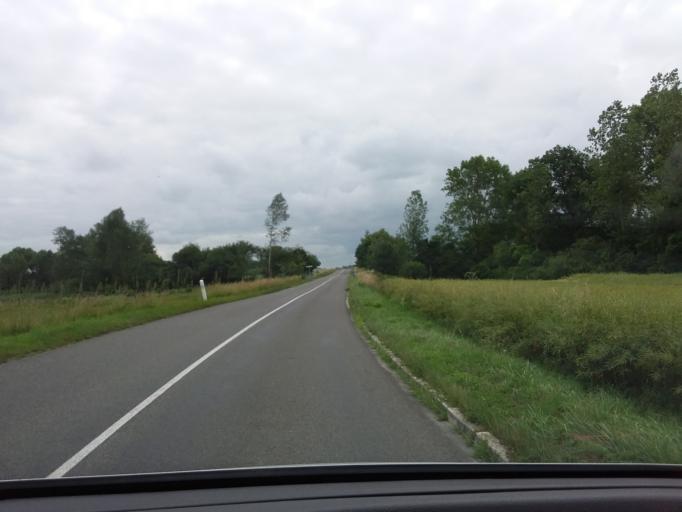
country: FR
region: Champagne-Ardenne
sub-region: Departement de la Marne
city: Cormicy
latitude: 49.4118
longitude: 3.8686
